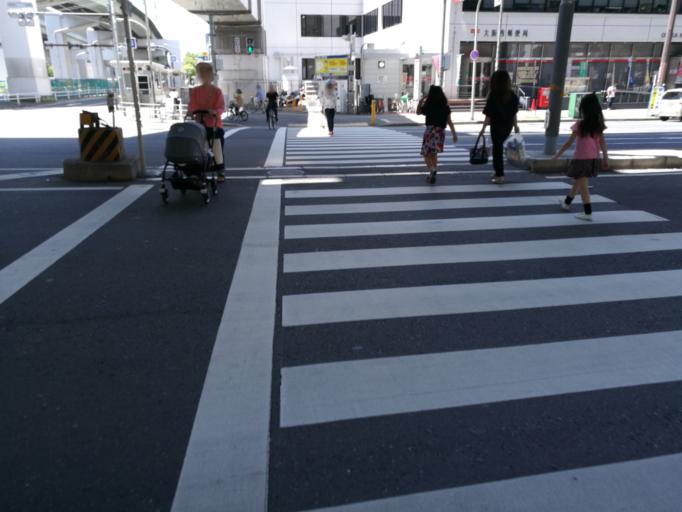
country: JP
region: Osaka
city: Osaka-shi
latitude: 34.6816
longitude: 135.4863
